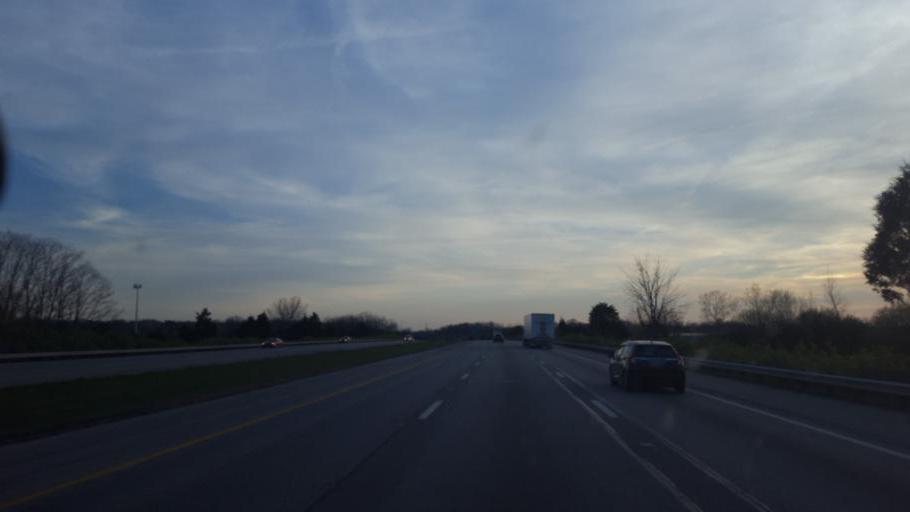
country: US
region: Ohio
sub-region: Warren County
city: Kings Mills
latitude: 39.3760
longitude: -84.2438
